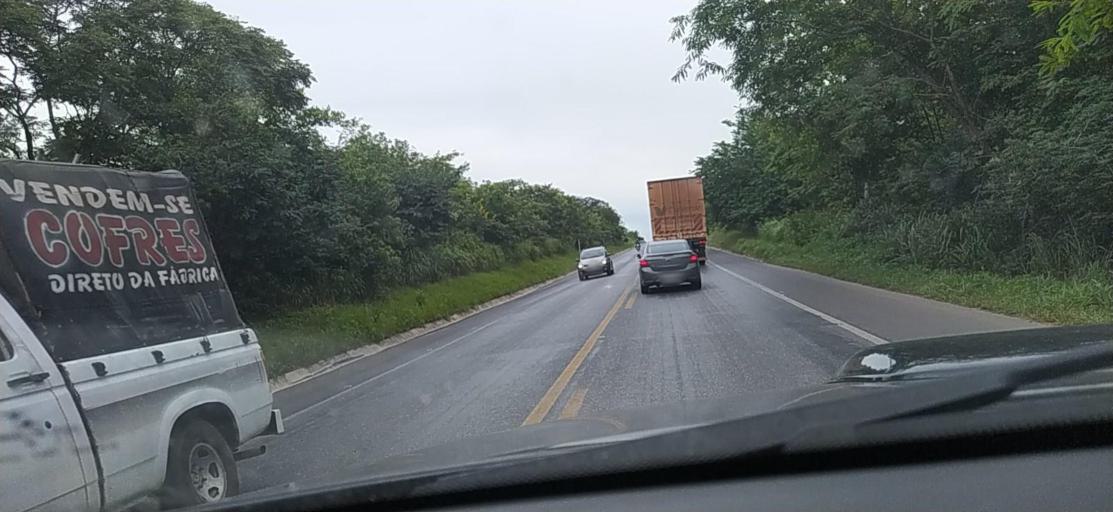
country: BR
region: Minas Gerais
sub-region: Montes Claros
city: Montes Claros
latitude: -16.6599
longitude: -43.7463
